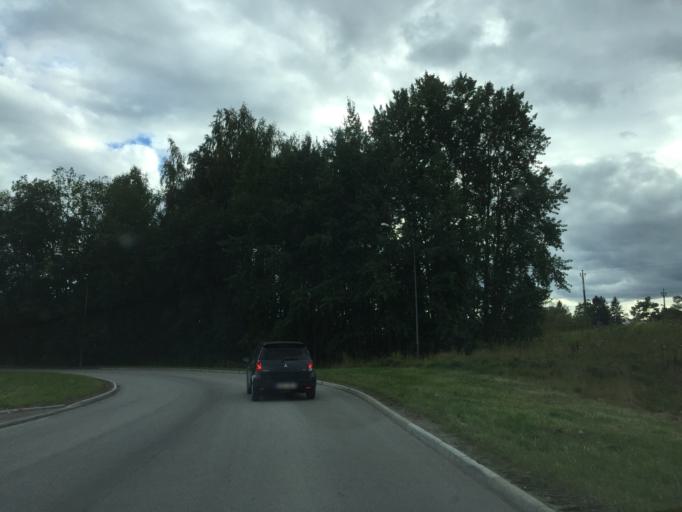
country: SE
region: OErebro
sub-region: Orebro Kommun
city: Hovsta
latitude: 59.3166
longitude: 15.2219
